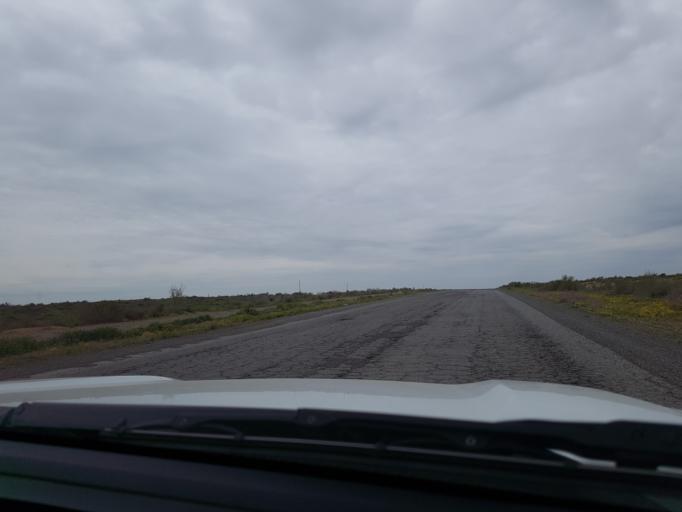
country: TM
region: Mary
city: Bayramaly
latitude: 37.9114
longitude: 62.6210
